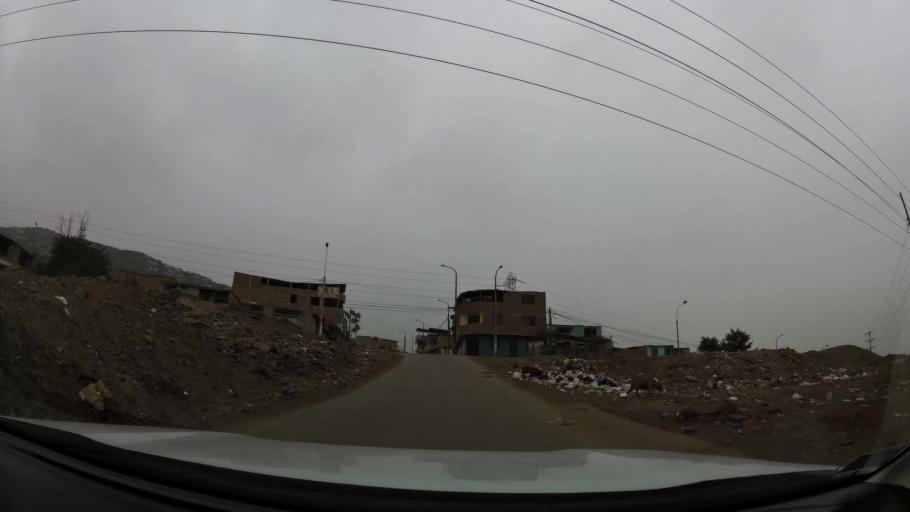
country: PE
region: Lima
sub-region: Lima
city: Surco
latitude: -12.2183
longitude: -76.9195
